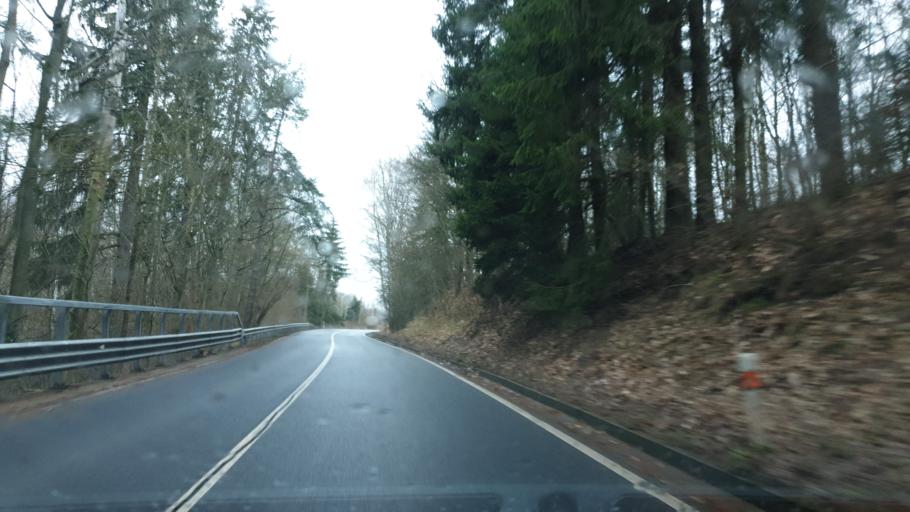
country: CZ
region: Karlovarsky
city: As
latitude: 50.2433
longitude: 12.1835
